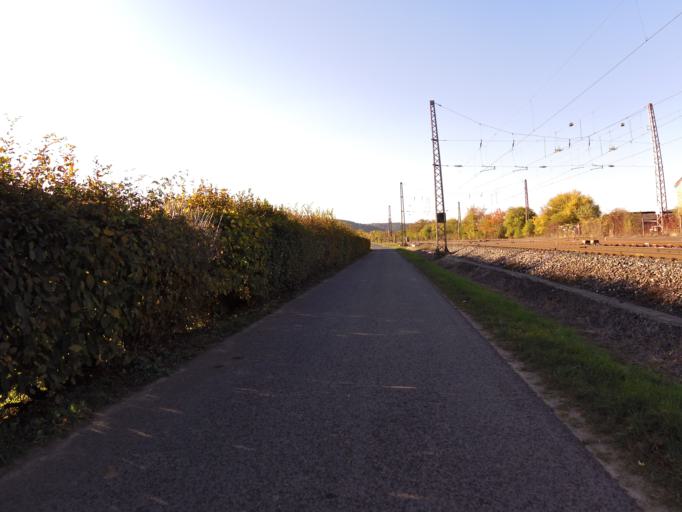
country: DE
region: Bavaria
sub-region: Regierungsbezirk Unterfranken
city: Winterhausen
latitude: 49.7122
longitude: 10.0067
